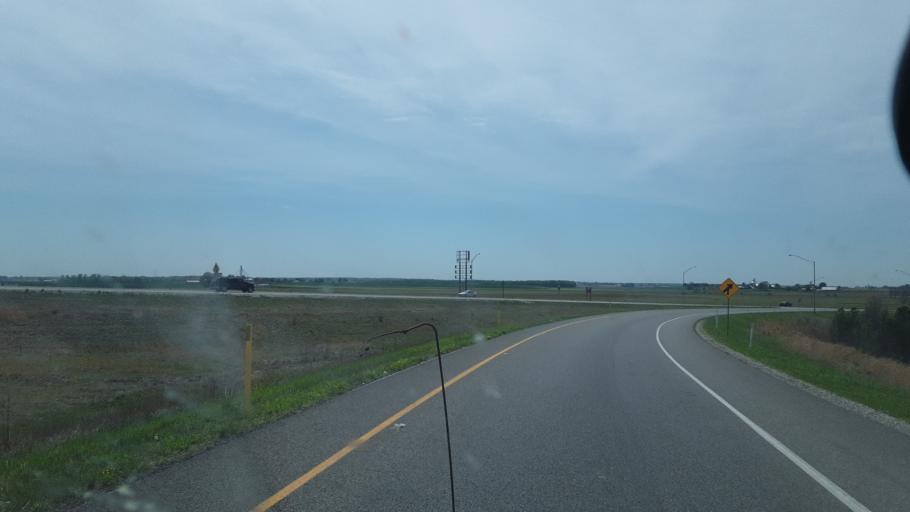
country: US
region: Indiana
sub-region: Gibson County
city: Haubstadt
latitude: 38.1684
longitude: -87.5523
